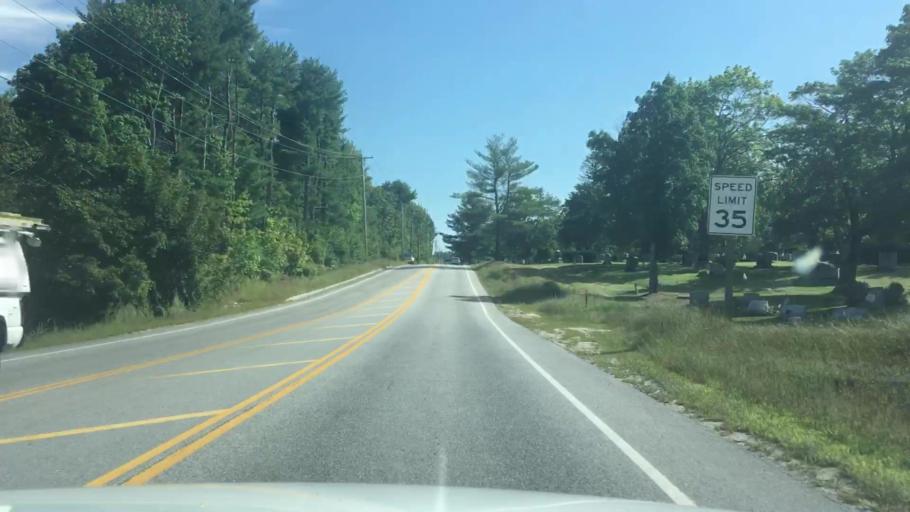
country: US
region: Maine
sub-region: Androscoggin County
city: Auburn
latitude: 44.1222
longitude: -70.2492
